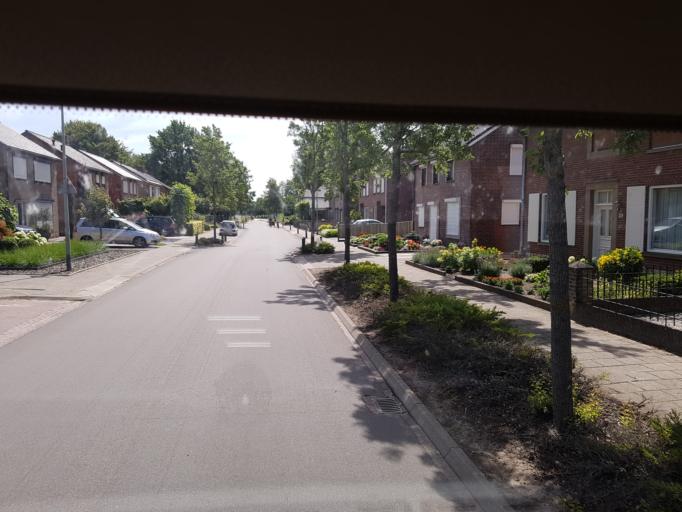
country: NL
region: Limburg
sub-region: Gemeente Leudal
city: Kelpen-Oler
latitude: 51.1884
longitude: 5.8141
